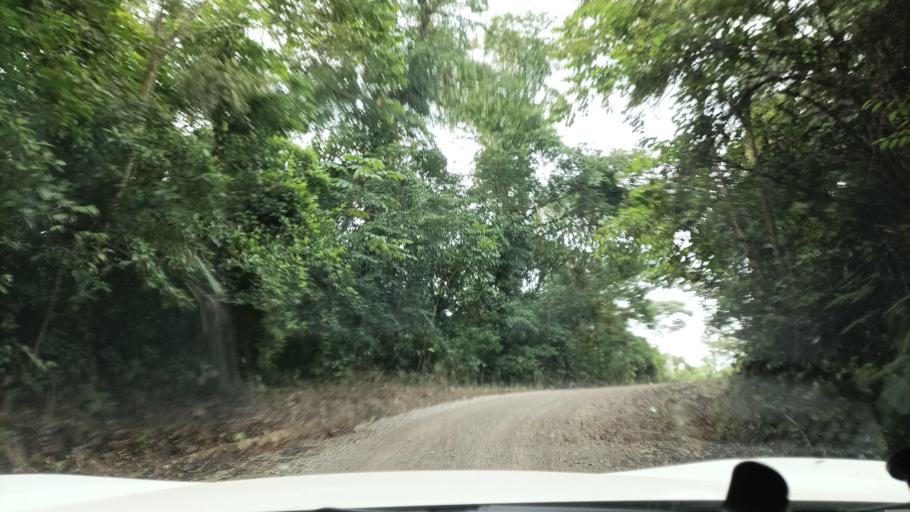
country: MX
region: Veracruz
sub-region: Uxpanapa
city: Poblado 10
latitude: 17.4313
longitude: -94.4182
